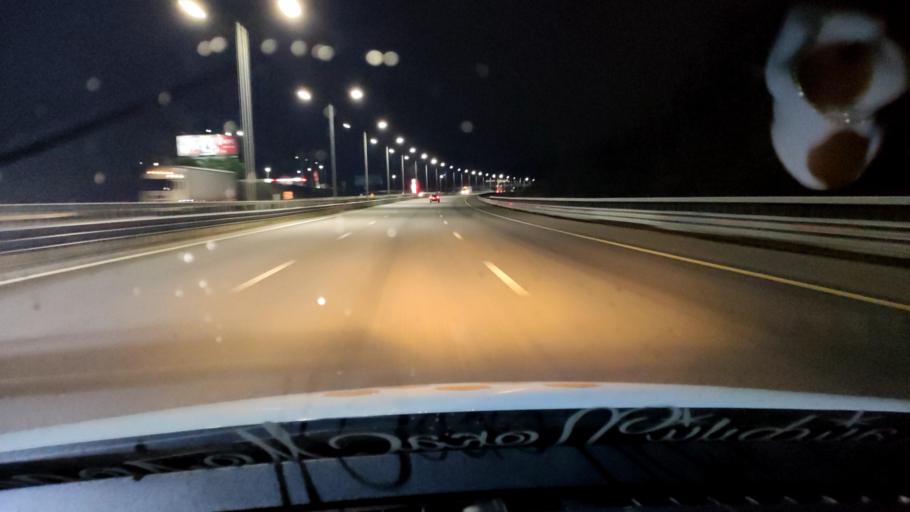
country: RU
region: Voronezj
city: Ramon'
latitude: 51.8277
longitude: 39.2463
